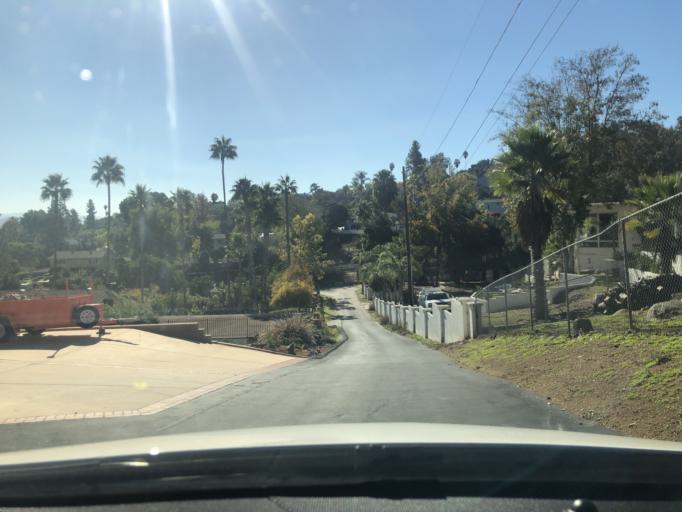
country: US
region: California
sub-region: San Diego County
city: Casa de Oro-Mount Helix
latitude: 32.7742
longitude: -116.9486
